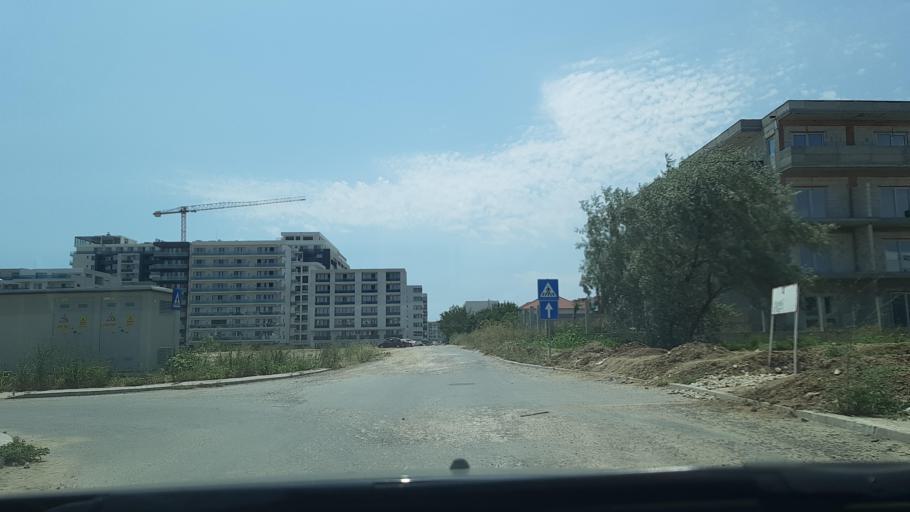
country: RO
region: Constanta
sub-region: Comuna Navodari
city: Navodari
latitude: 44.2969
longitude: 28.6232
